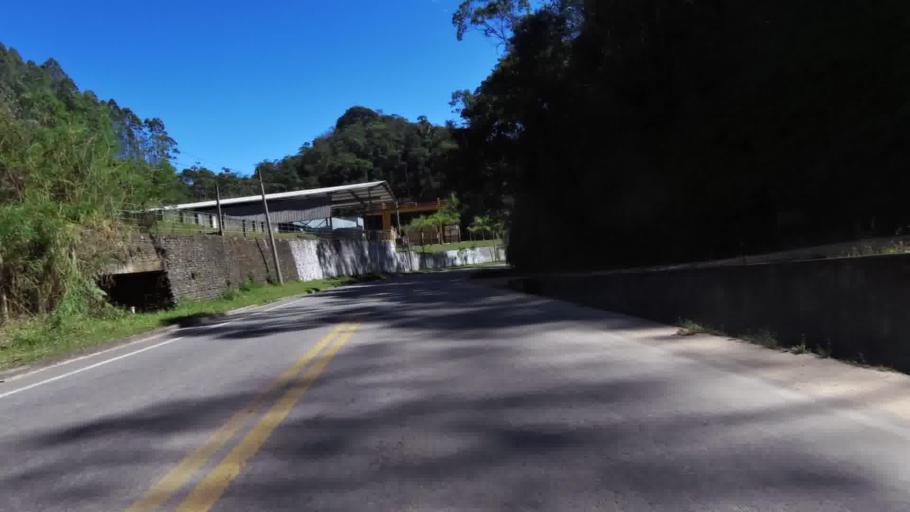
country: BR
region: Espirito Santo
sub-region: Vargem Alta
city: Vargem Alta
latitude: -20.6652
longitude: -40.9618
